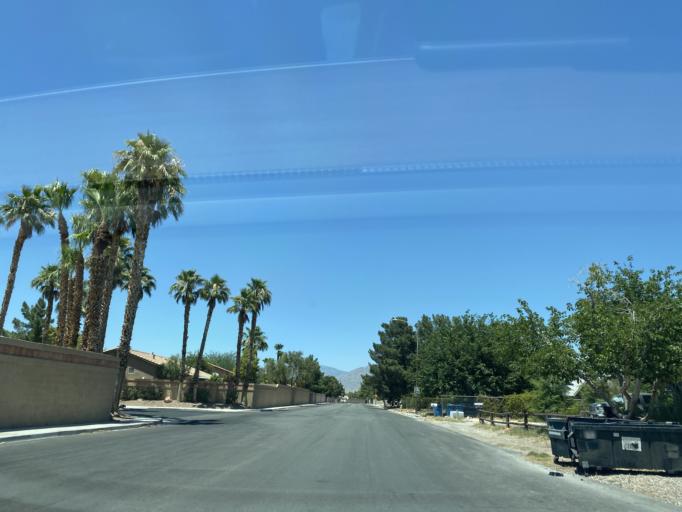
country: US
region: Nevada
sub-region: Clark County
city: Las Vegas
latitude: 36.2288
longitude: -115.2122
